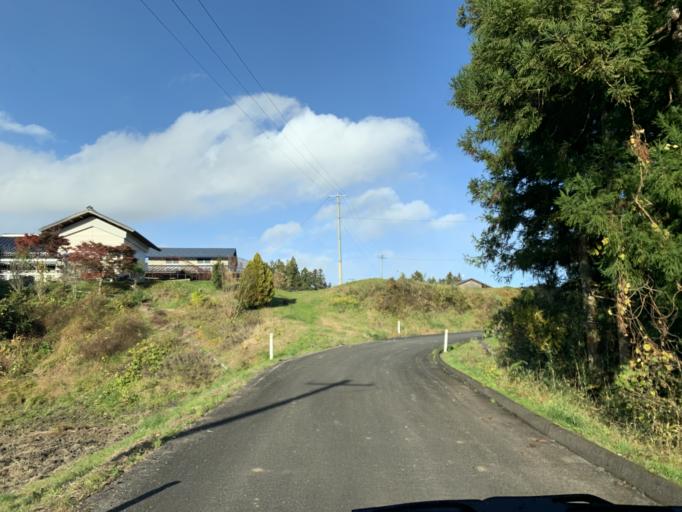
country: JP
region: Iwate
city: Ichinoseki
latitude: 39.0119
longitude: 141.0833
